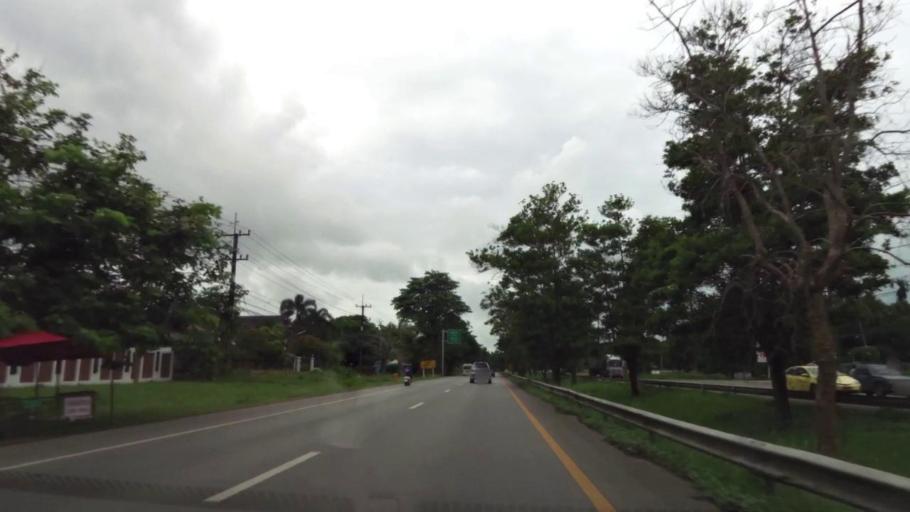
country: TH
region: Chanthaburi
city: Tha Mai
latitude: 12.6486
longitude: 102.0253
